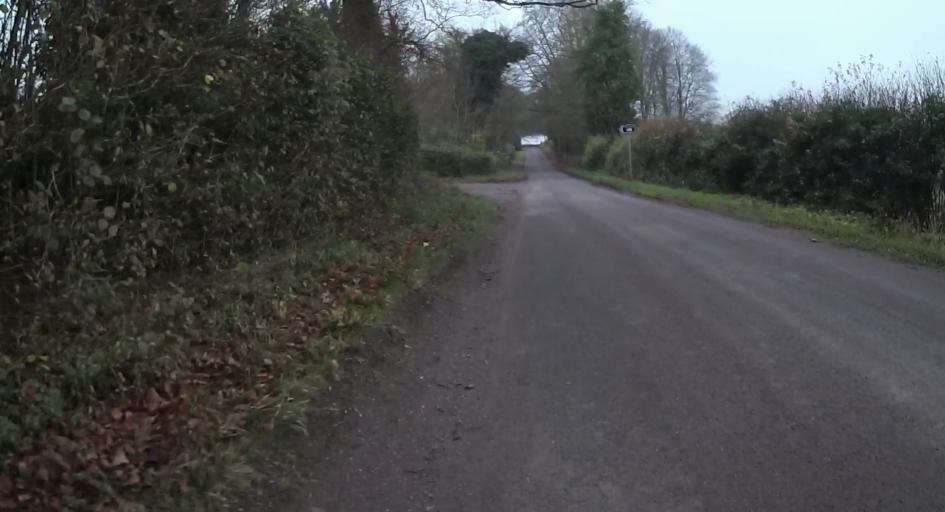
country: GB
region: England
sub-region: Hampshire
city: Kings Worthy
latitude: 51.1278
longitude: -1.2114
